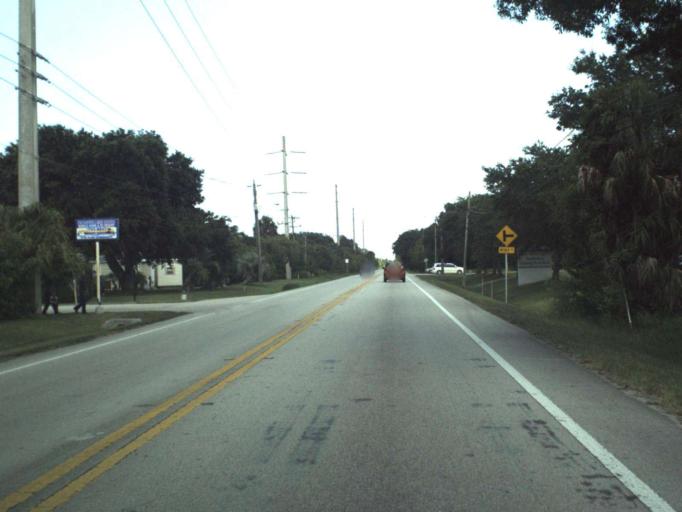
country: US
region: Florida
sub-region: Brevard County
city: Palm Bay
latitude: 27.9983
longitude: -80.6073
